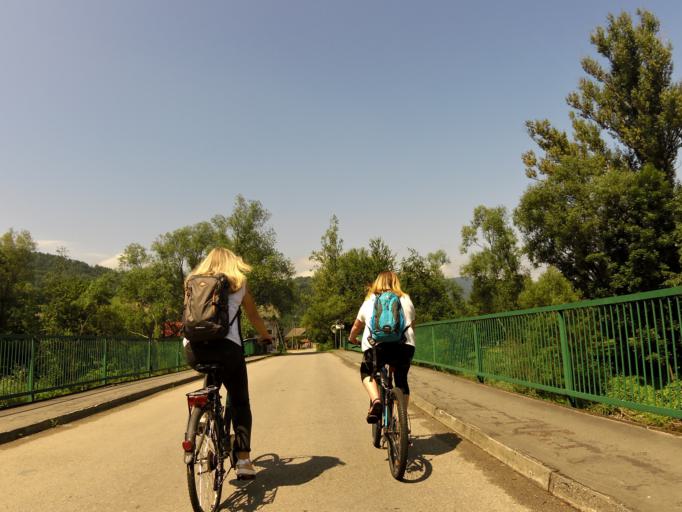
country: PL
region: Silesian Voivodeship
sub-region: Powiat zywiecki
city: Milowka
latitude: 49.5719
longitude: 19.0934
